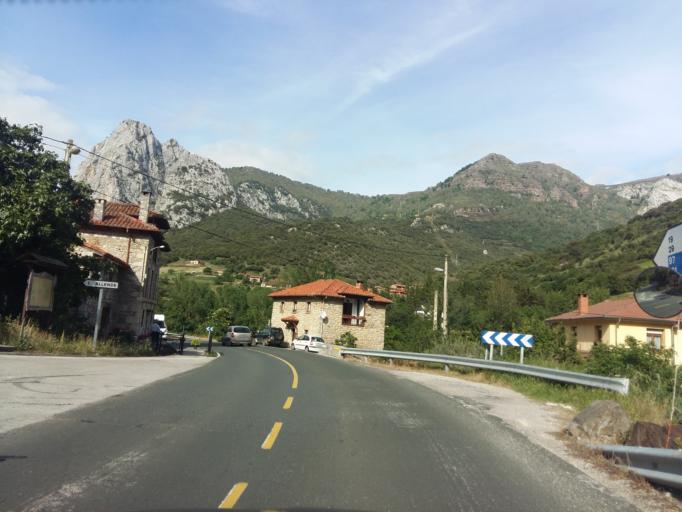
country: ES
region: Cantabria
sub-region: Provincia de Cantabria
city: Potes
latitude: 43.2129
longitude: -4.5928
